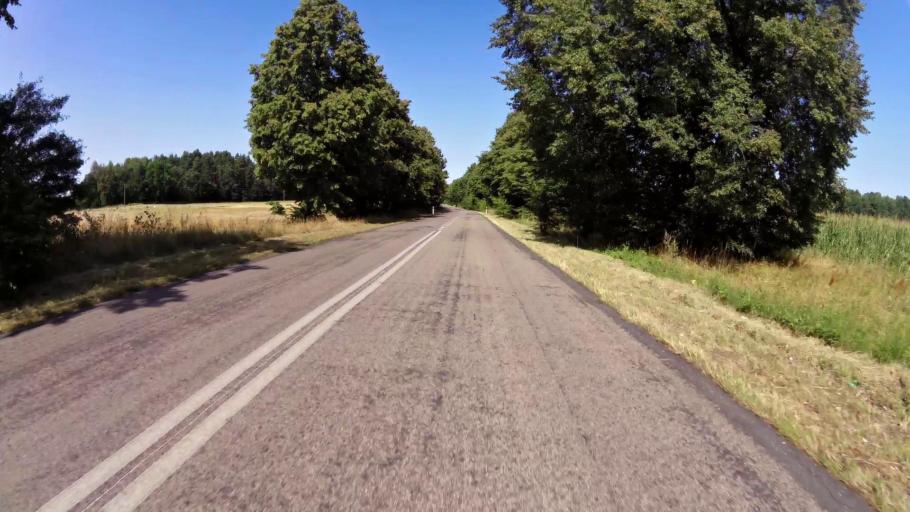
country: PL
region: West Pomeranian Voivodeship
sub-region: Powiat stargardzki
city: Dobrzany
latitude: 53.3307
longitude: 15.3919
